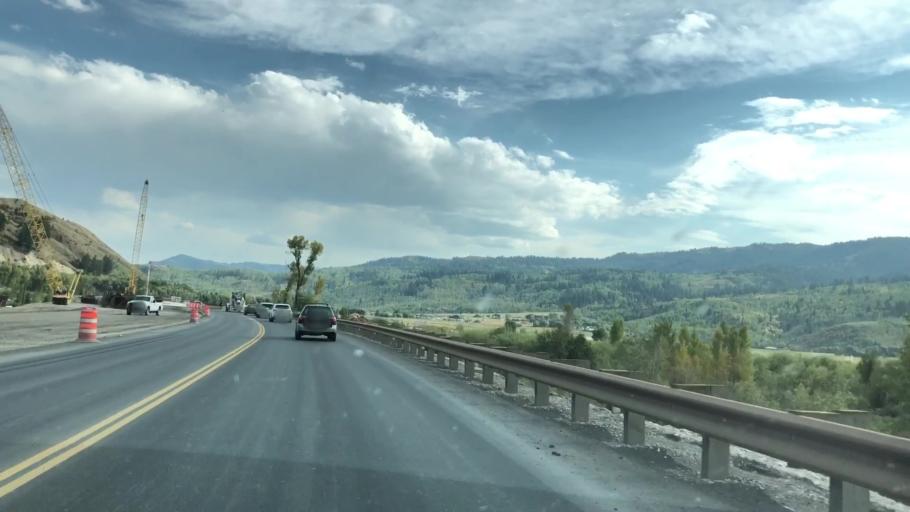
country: US
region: Wyoming
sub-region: Teton County
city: South Park
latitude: 43.3870
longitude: -110.7466
